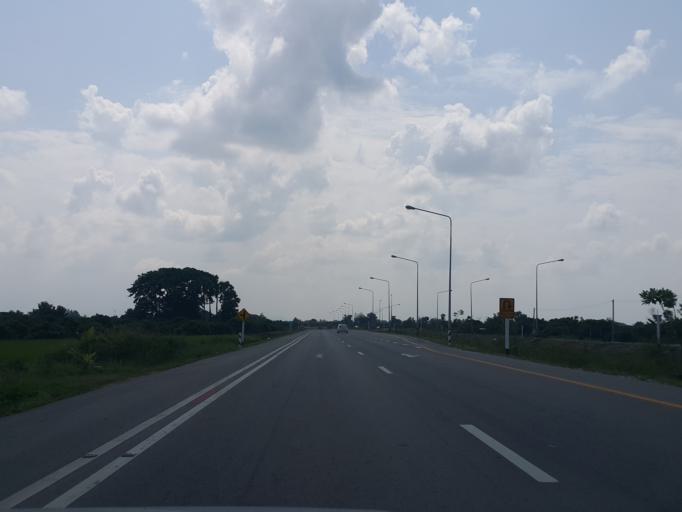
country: TH
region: Chiang Mai
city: San Pa Tong
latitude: 18.5534
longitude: 98.8496
